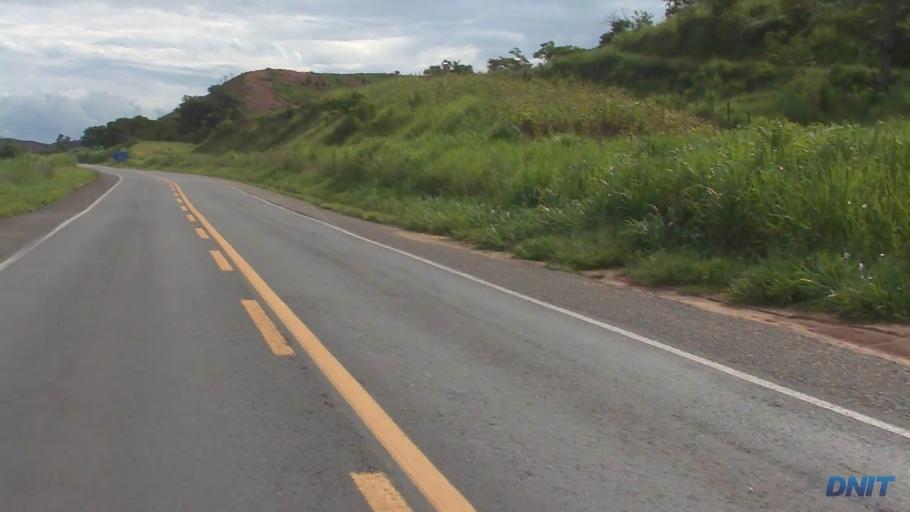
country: BR
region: Minas Gerais
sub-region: Belo Oriente
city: Belo Oriente
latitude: -19.1903
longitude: -42.2724
